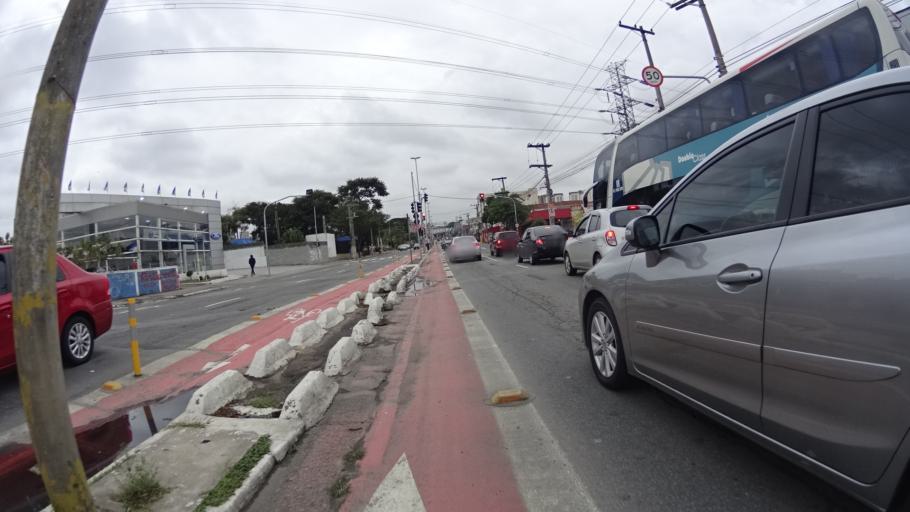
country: BR
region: Sao Paulo
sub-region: Sao Paulo
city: Sao Paulo
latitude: -23.5077
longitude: -46.6155
